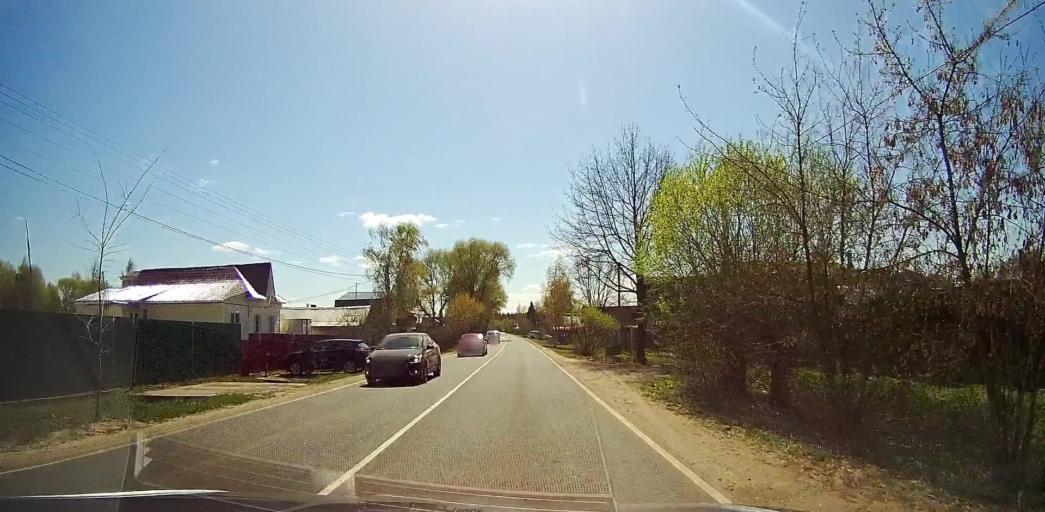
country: RU
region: Moskovskaya
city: Beloozerskiy
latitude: 55.5087
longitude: 38.4311
